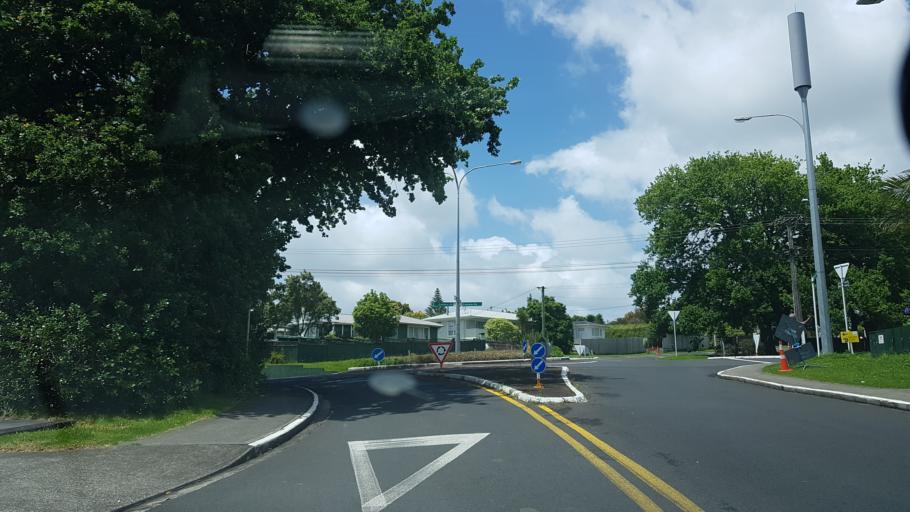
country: NZ
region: Auckland
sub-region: Auckland
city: North Shore
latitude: -36.7930
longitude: 174.7072
